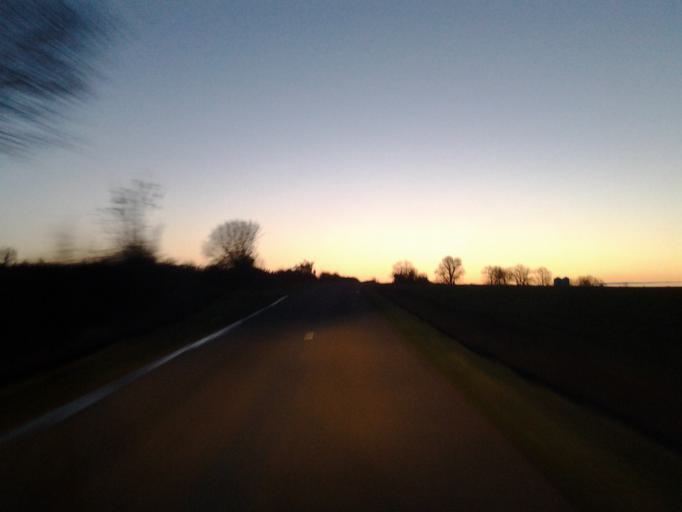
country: FR
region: Pays de la Loire
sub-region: Departement de la Vendee
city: La Roche-sur-Yon
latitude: 46.6584
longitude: -1.4128
